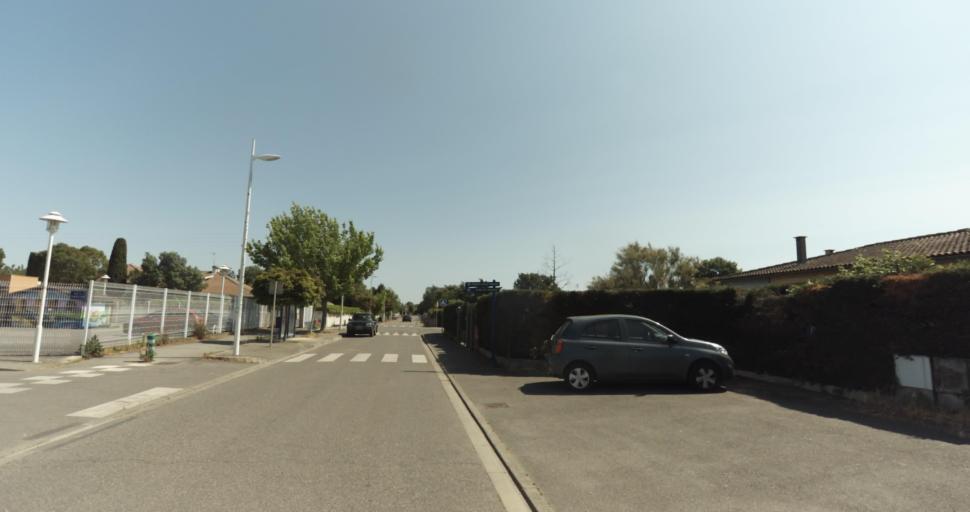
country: FR
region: Midi-Pyrenees
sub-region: Departement de la Haute-Garonne
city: Plaisance-du-Touch
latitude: 43.5749
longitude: 1.2868
